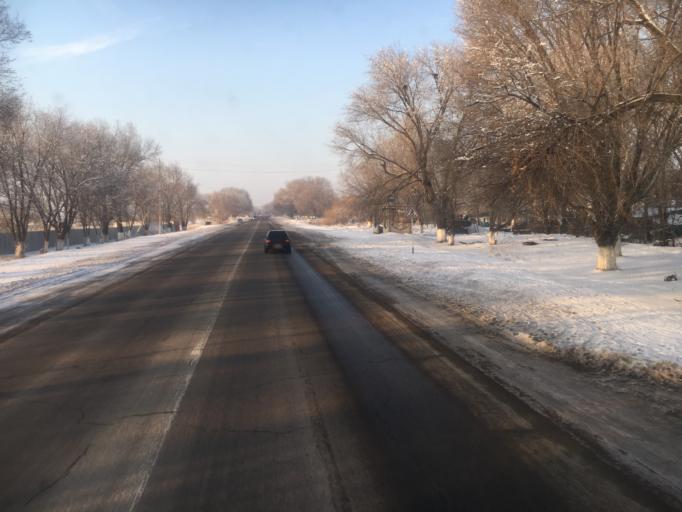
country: KZ
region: Almaty Oblysy
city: Burunday
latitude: 43.3360
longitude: 76.6601
